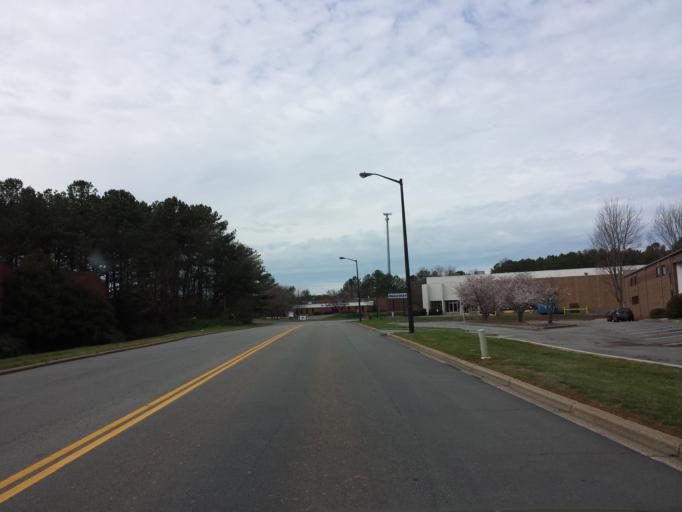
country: US
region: Georgia
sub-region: Cobb County
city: Marietta
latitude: 33.9753
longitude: -84.5308
